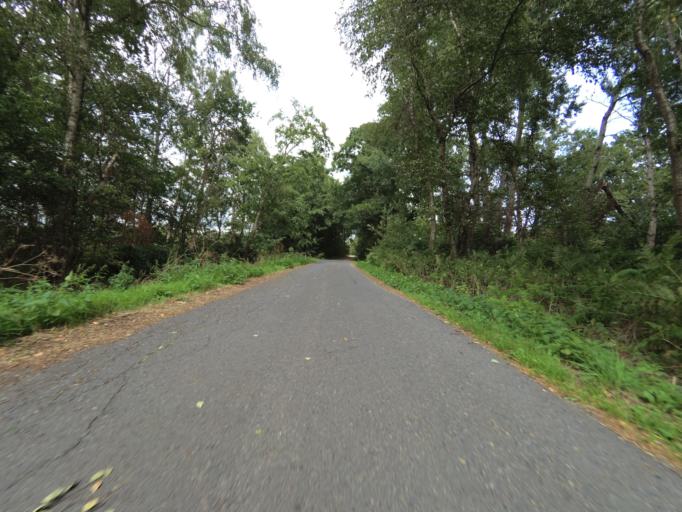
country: DE
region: North Rhine-Westphalia
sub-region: Regierungsbezirk Munster
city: Gronau
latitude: 52.1824
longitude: 6.9658
